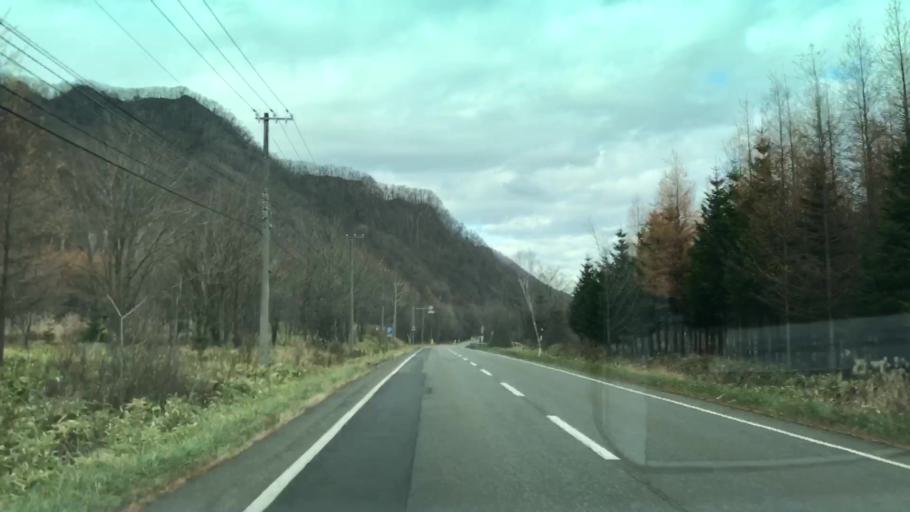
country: JP
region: Hokkaido
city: Shizunai-furukawacho
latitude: 42.8341
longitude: 142.4158
